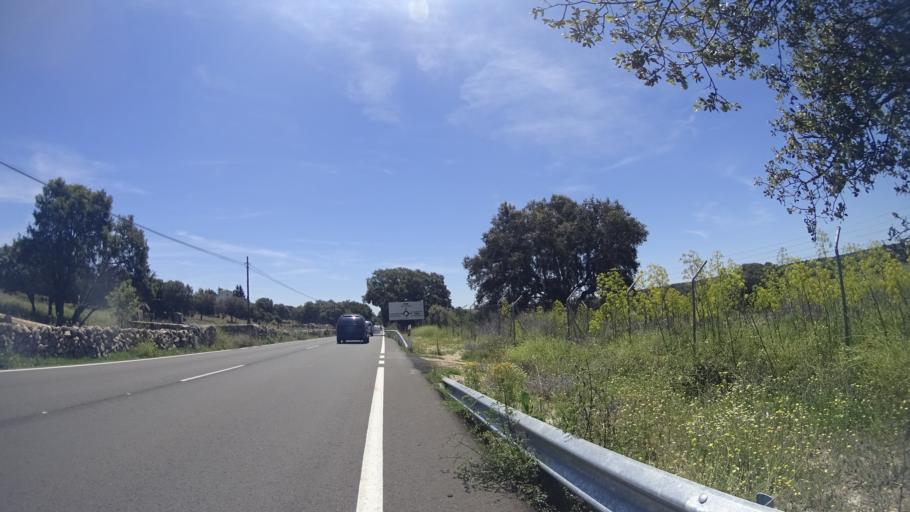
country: ES
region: Madrid
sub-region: Provincia de Madrid
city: Galapagar
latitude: 40.5953
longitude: -4.0148
